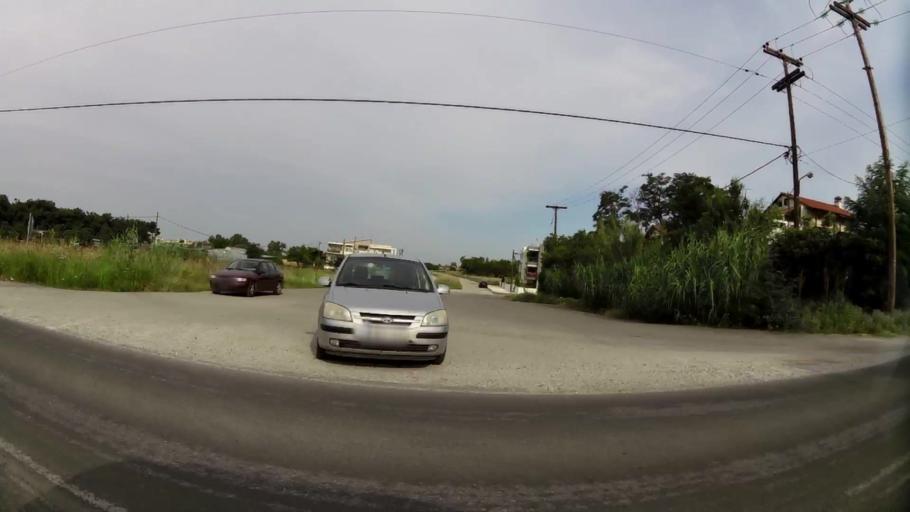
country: GR
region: Central Macedonia
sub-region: Nomos Thessalonikis
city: Thermi
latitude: 40.5550
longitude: 23.0189
